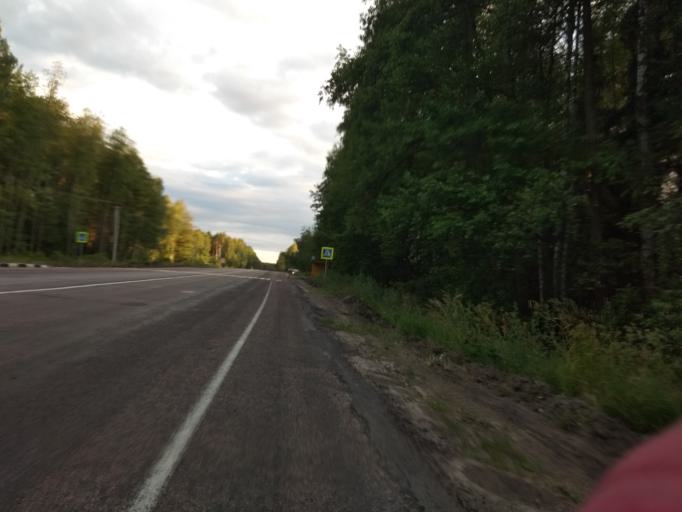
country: RU
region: Moskovskaya
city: Misheronskiy
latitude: 55.6348
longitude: 39.7471
